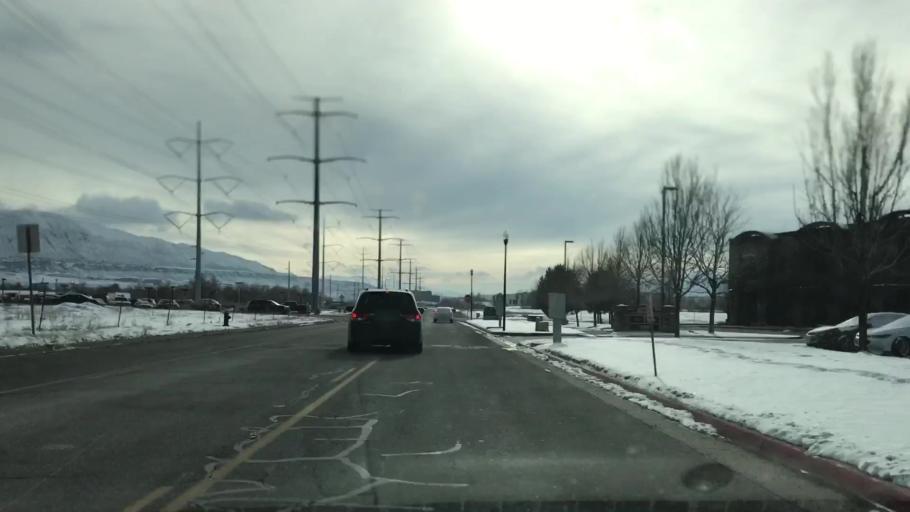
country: US
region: Utah
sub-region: Salt Lake County
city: Draper
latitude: 40.5223
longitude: -111.8946
